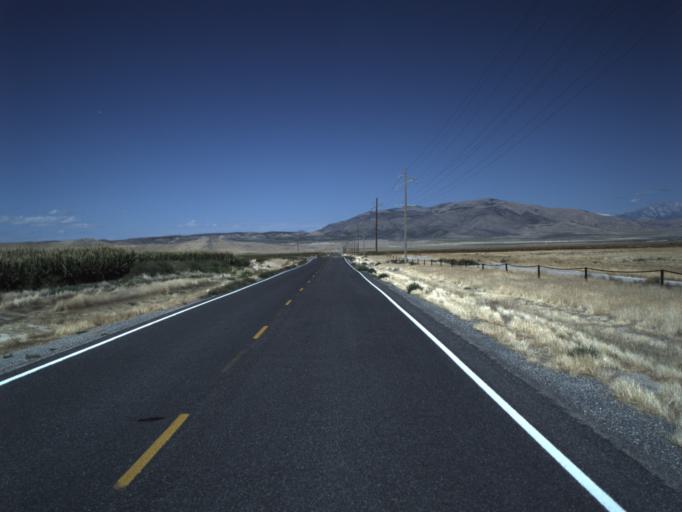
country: US
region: Utah
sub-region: Utah County
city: Genola
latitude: 40.0863
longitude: -111.9588
